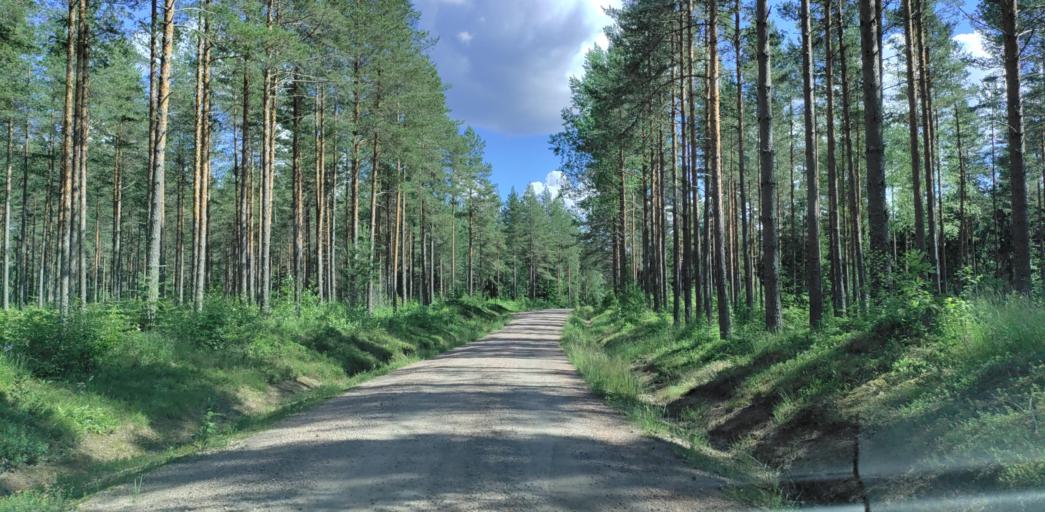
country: SE
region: Vaermland
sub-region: Munkfors Kommun
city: Munkfors
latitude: 59.9510
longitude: 13.5024
